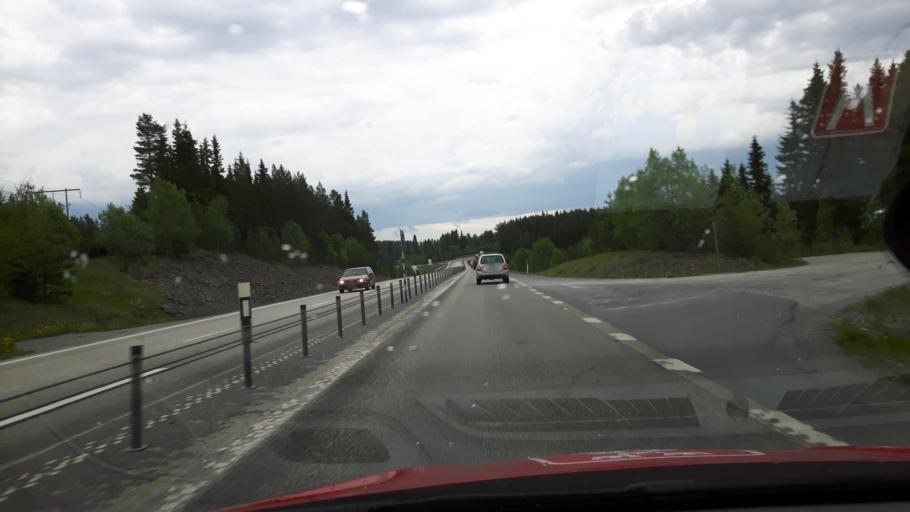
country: SE
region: Jaemtland
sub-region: OEstersunds Kommun
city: Brunflo
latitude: 63.1222
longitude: 14.7952
